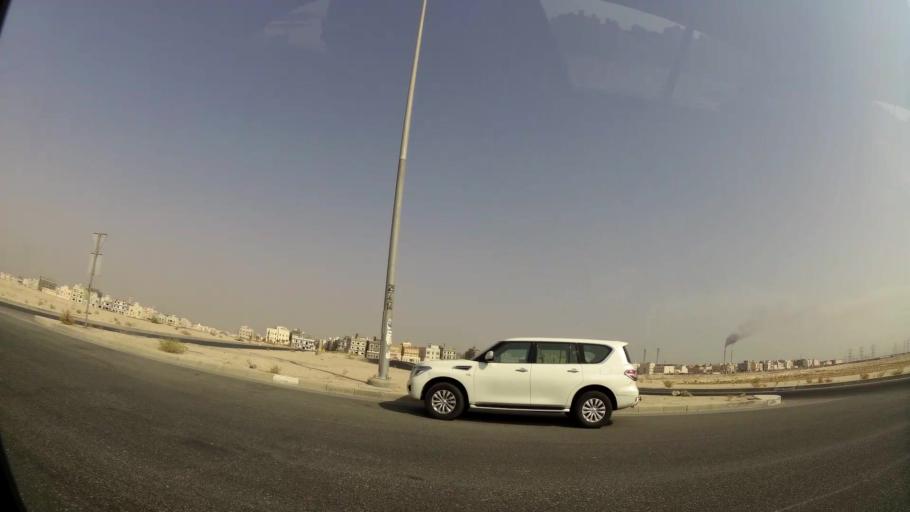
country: KW
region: Muhafazat al Jahra'
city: Al Jahra'
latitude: 29.3419
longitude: 47.7698
